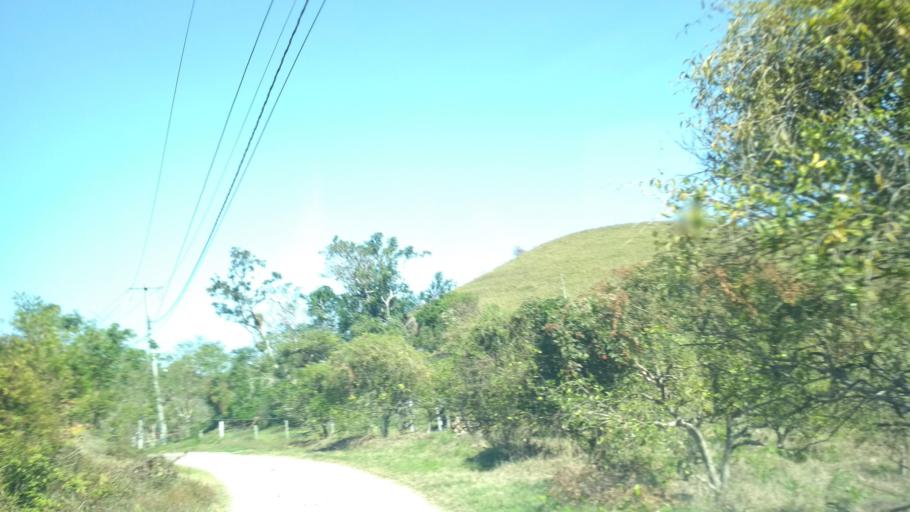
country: MX
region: Veracruz
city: Gutierrez Zamora
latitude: 20.4931
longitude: -97.1665
